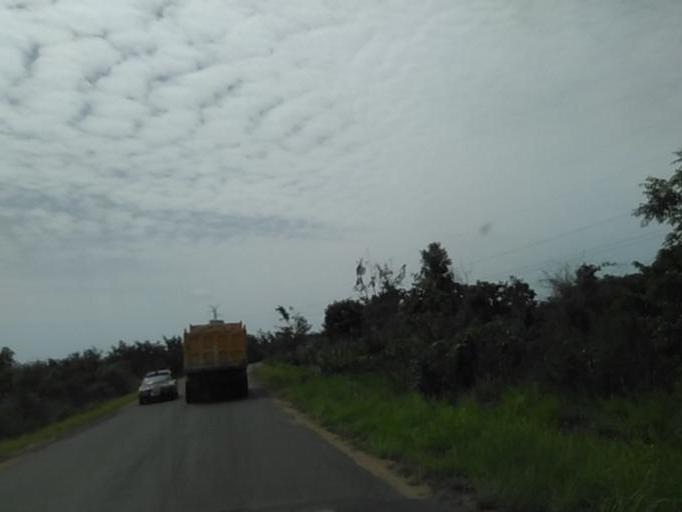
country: GH
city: Akropong
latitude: 6.0954
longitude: 0.0583
